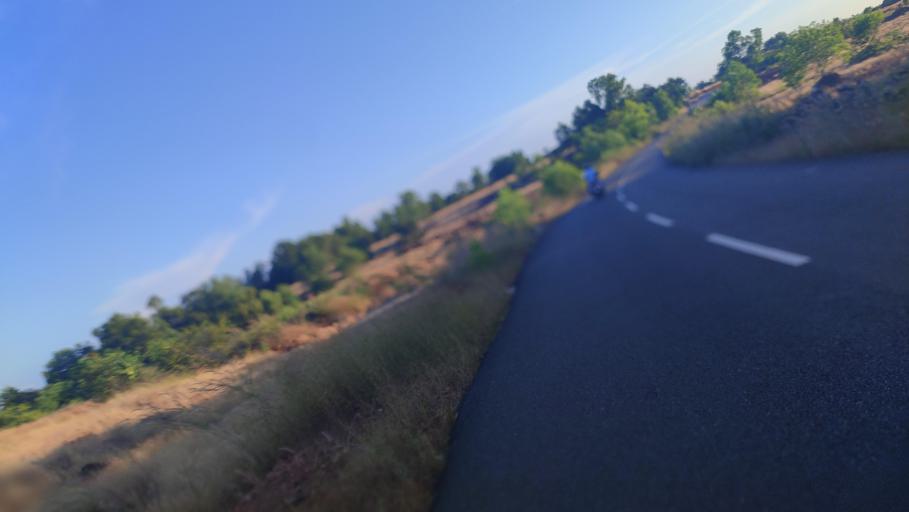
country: IN
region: Kerala
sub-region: Kasaragod District
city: Kasaragod
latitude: 12.4464
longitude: 75.0994
